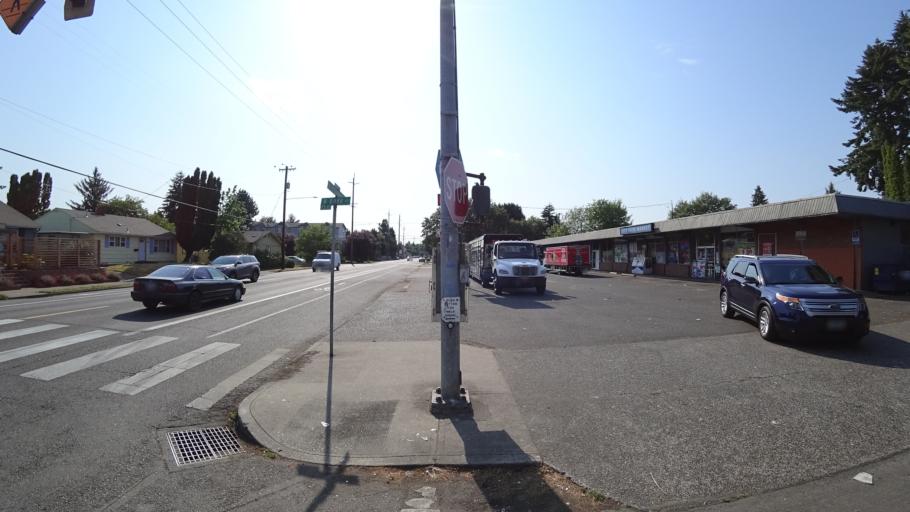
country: US
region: Oregon
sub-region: Washington County
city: West Haven
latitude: 45.5941
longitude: -122.7384
